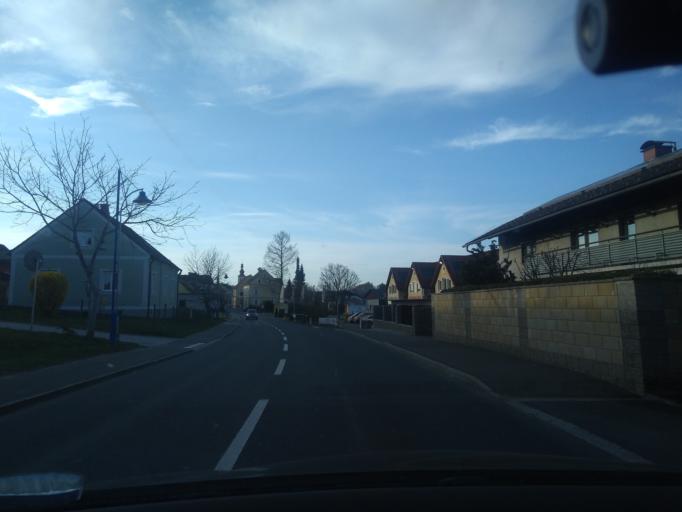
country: AT
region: Styria
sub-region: Politischer Bezirk Suedoststeiermark
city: Kirchbach in Steiermark
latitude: 46.9276
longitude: 15.6662
